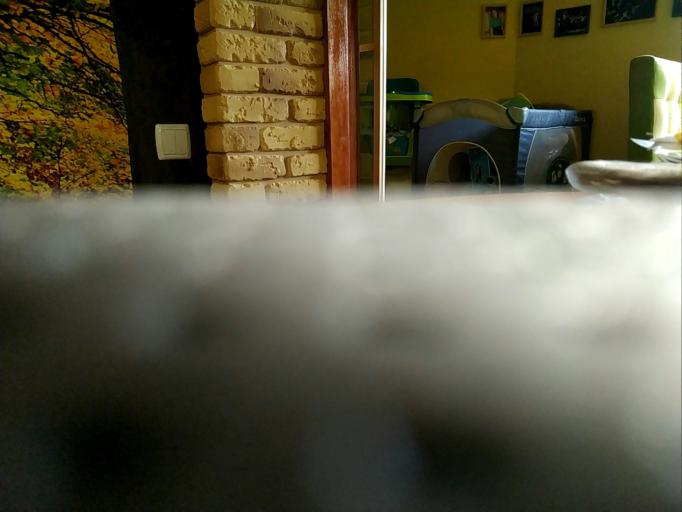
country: RU
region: Kaluga
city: Seredeyskiy
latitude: 53.9325
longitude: 35.3431
